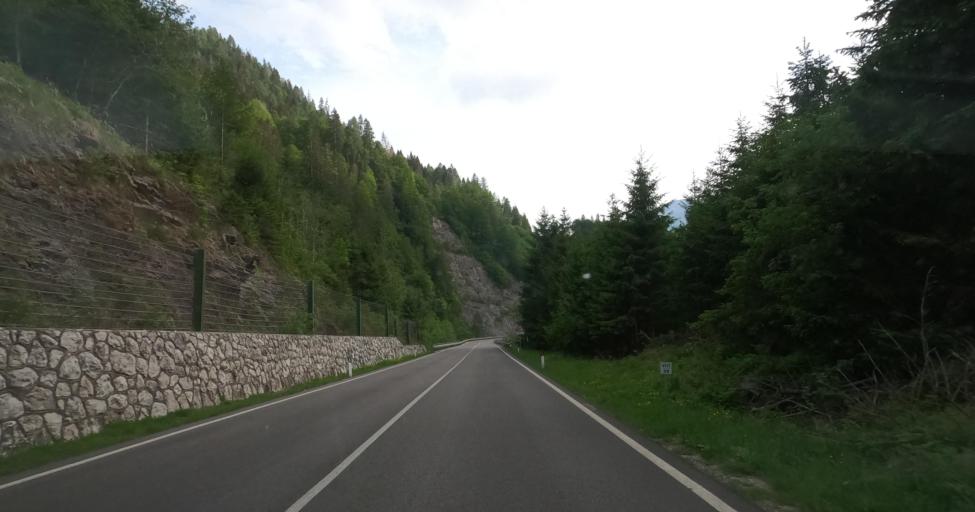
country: IT
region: Veneto
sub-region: Provincia di Belluno
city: Celat-San Tomaso Agordino
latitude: 46.3739
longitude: 11.9816
